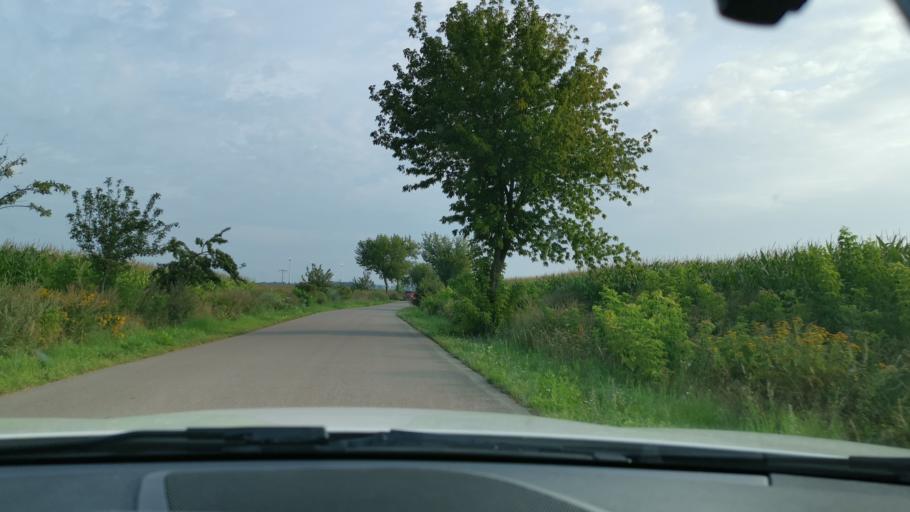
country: DE
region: Brandenburg
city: Juterbog
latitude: 51.9400
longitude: 13.1378
